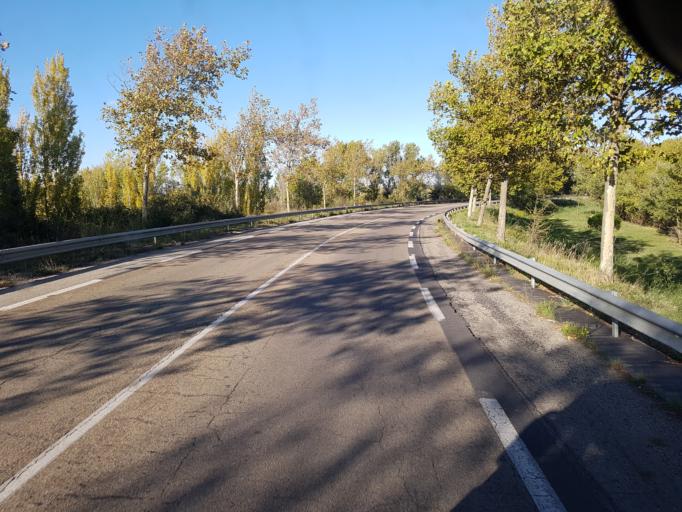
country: FR
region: Languedoc-Roussillon
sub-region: Departement de l'Aude
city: Coursan
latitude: 43.2406
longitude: 3.0600
